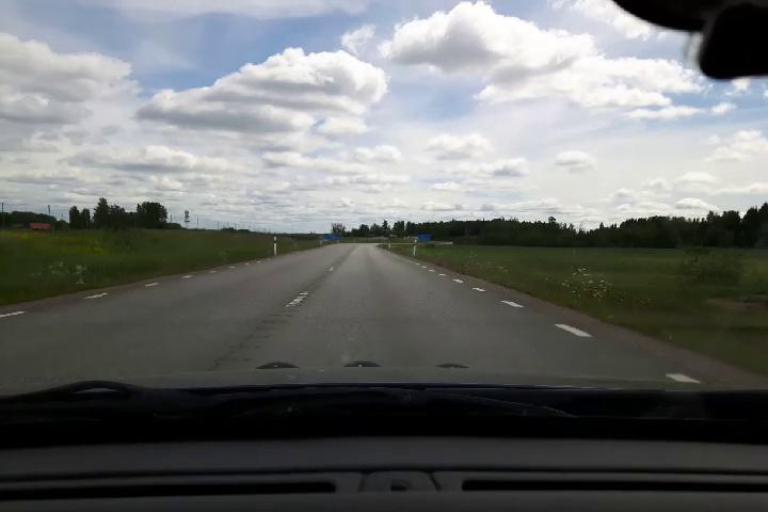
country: SE
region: Uppsala
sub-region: Tierps Kommun
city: Tierp
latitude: 60.3442
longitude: 17.4789
